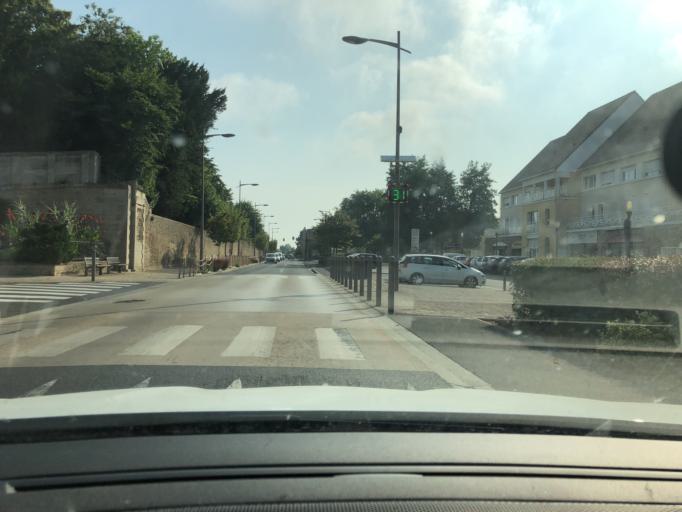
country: FR
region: Lower Normandy
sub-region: Departement du Calvados
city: Douvres-la-Delivrande
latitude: 49.2970
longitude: -0.3735
